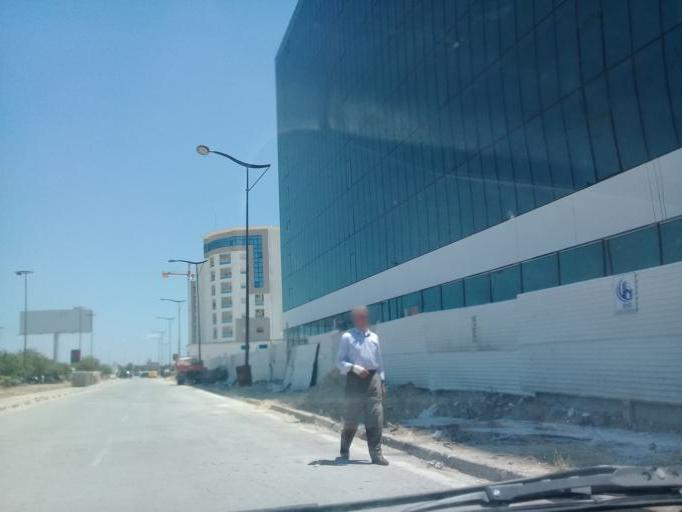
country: TN
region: Tunis
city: La Goulette
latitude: 36.8495
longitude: 10.2755
